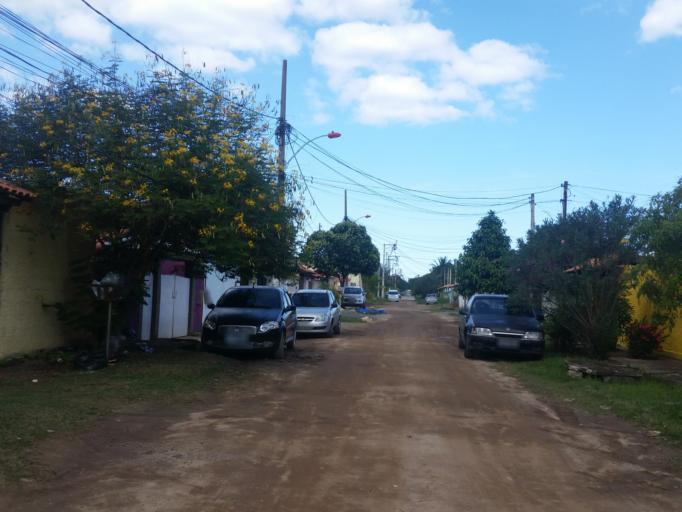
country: BR
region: Rio de Janeiro
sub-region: Marica
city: Marica
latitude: -22.9580
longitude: -42.9667
